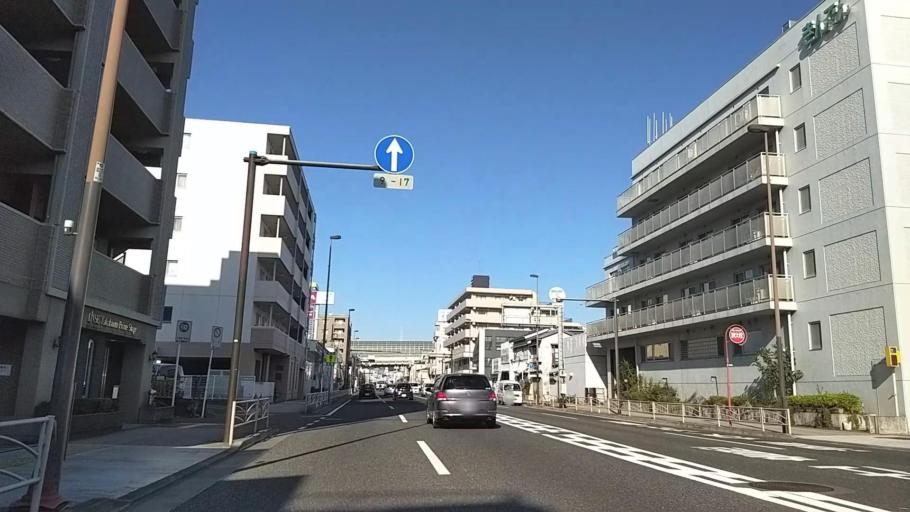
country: JP
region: Kanagawa
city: Yokohama
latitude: 35.4628
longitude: 139.5933
